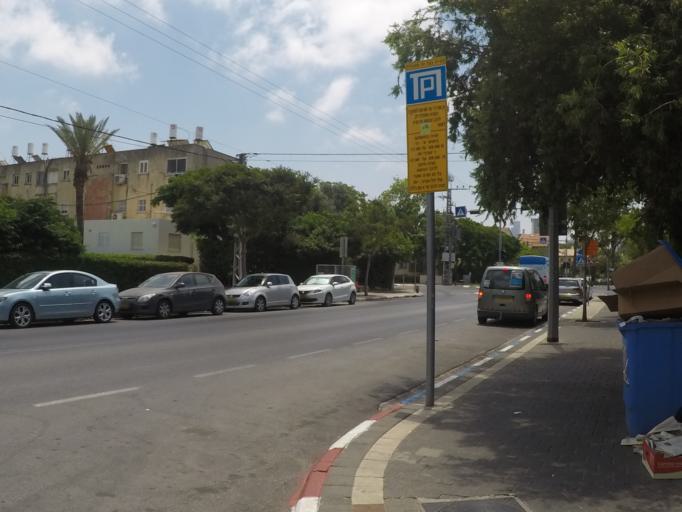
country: IL
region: Tel Aviv
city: Tel Aviv
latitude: 32.1059
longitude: 34.7943
